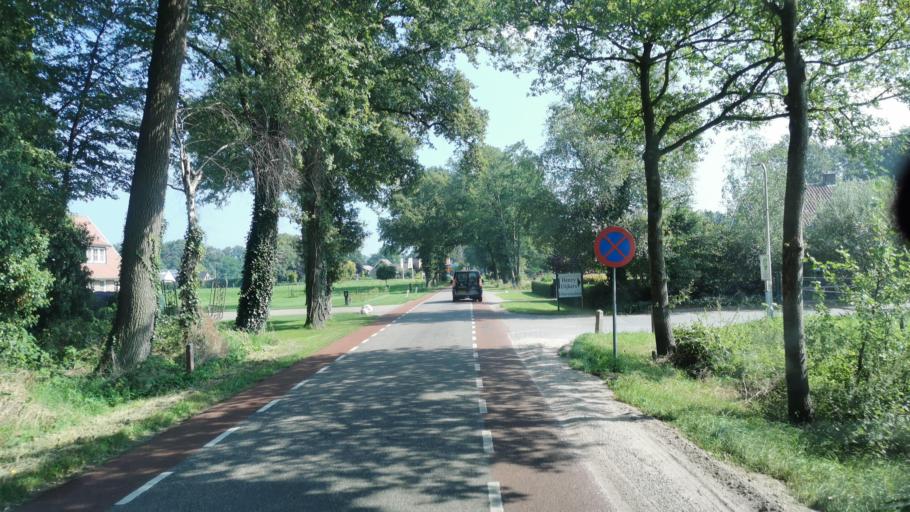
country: NL
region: Overijssel
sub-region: Gemeente Tubbergen
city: Tubbergen
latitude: 52.3512
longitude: 6.8292
